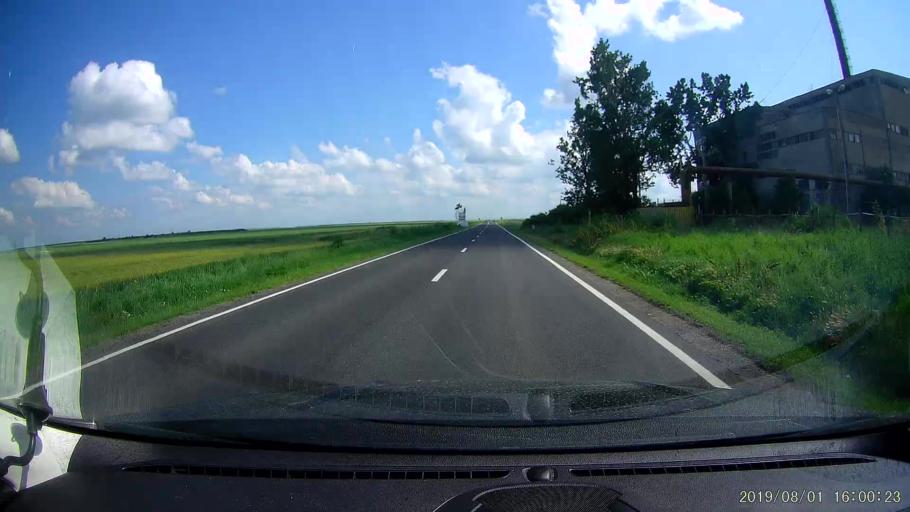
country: RO
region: Ialomita
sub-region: Comuna Ciulnita
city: Ciulnita
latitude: 44.5305
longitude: 27.3885
